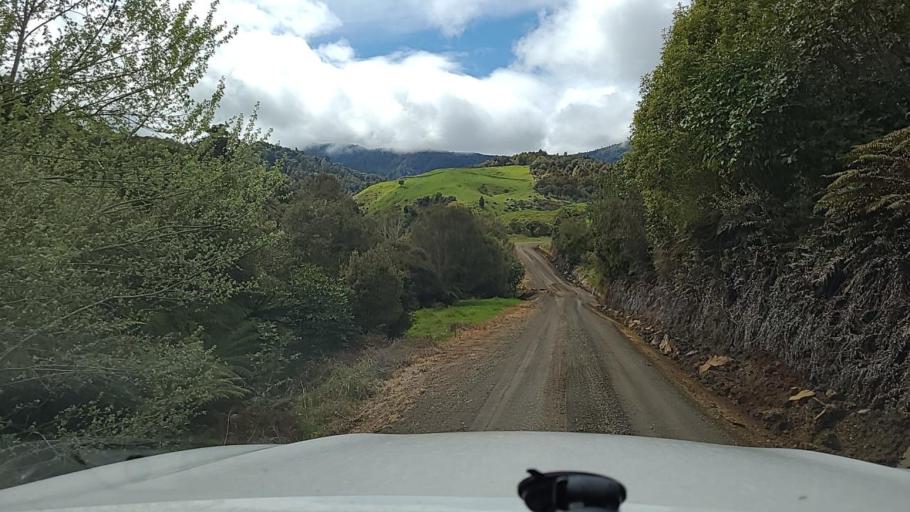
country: NZ
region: Bay of Plenty
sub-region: Opotiki District
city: Opotiki
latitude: -38.2509
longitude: 177.5993
